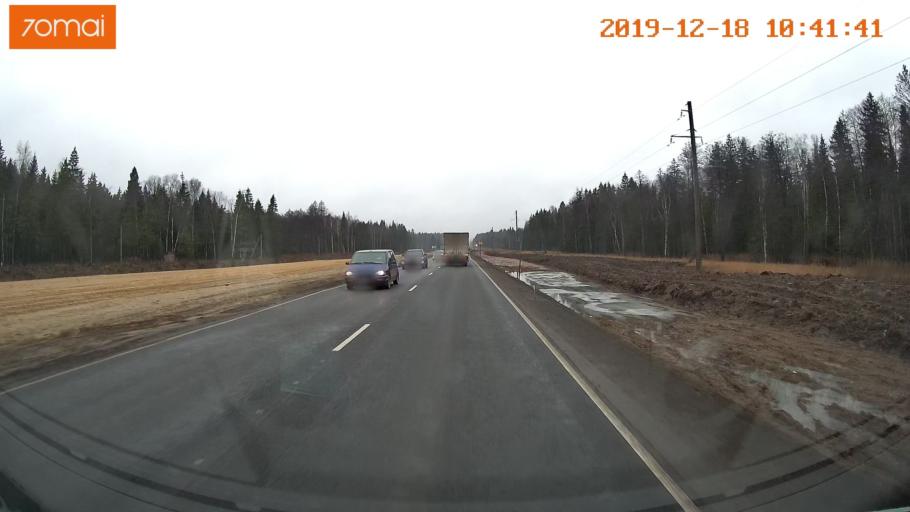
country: RU
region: Moskovskaya
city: Aprelevka
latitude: 55.4576
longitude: 37.1077
